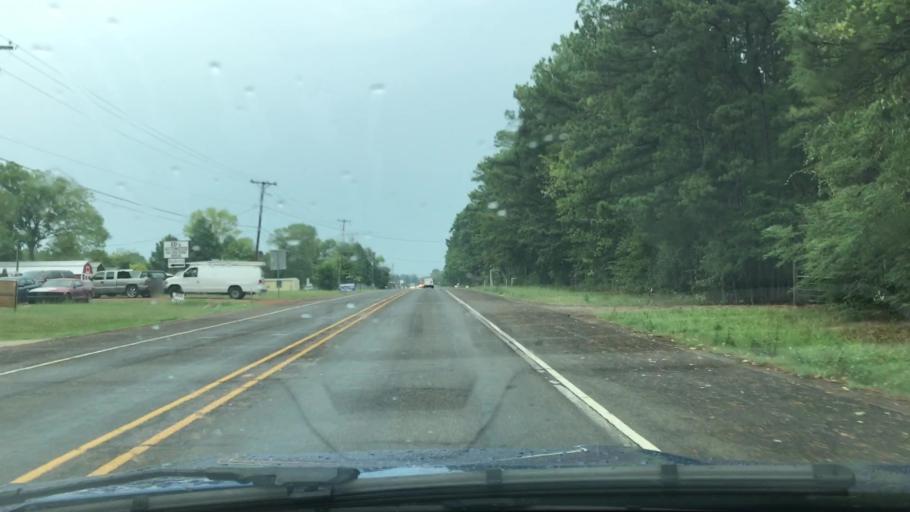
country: US
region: Texas
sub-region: Harrison County
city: Waskom
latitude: 32.4738
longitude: -94.0484
